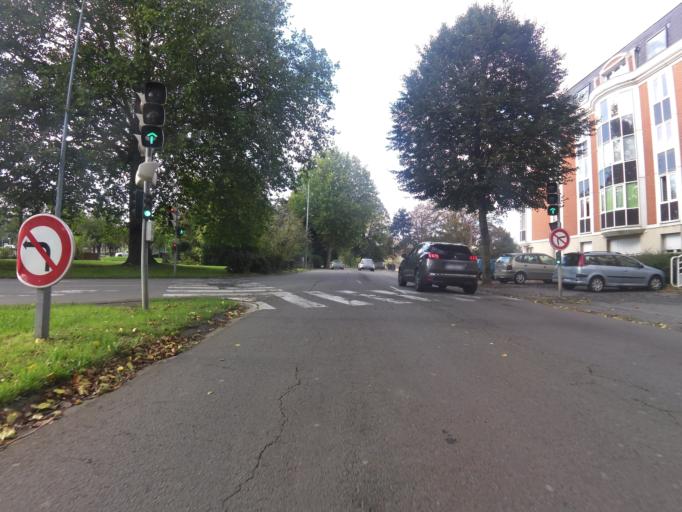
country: FR
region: Nord-Pas-de-Calais
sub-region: Departement du Nord
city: Neuville-Saint-Remy
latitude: 50.1742
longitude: 3.2233
